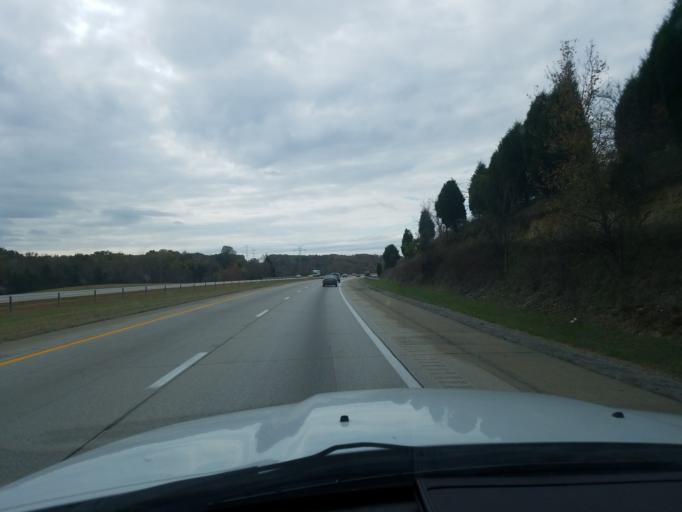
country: US
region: Kentucky
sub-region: Jefferson County
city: Jeffersontown
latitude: 38.1646
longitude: -85.5219
